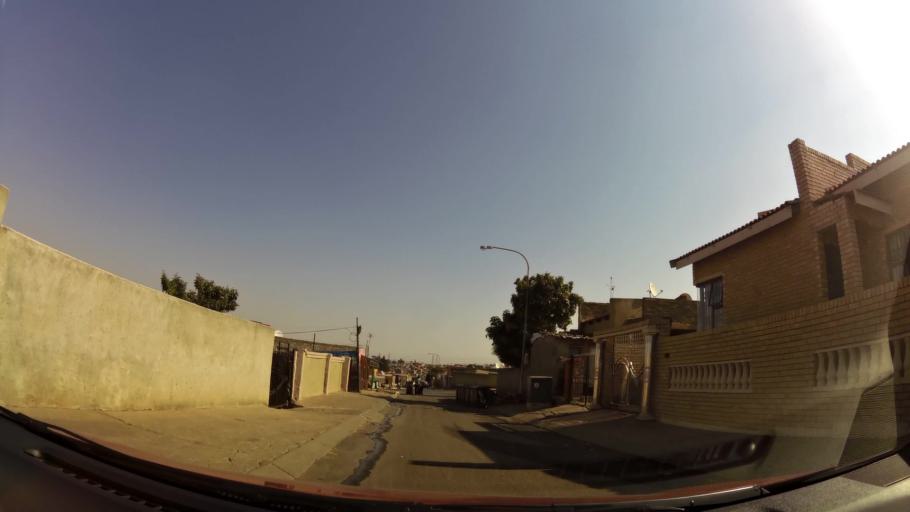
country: ZA
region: Gauteng
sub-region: City of Johannesburg Metropolitan Municipality
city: Soweto
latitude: -26.2511
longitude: 27.9396
